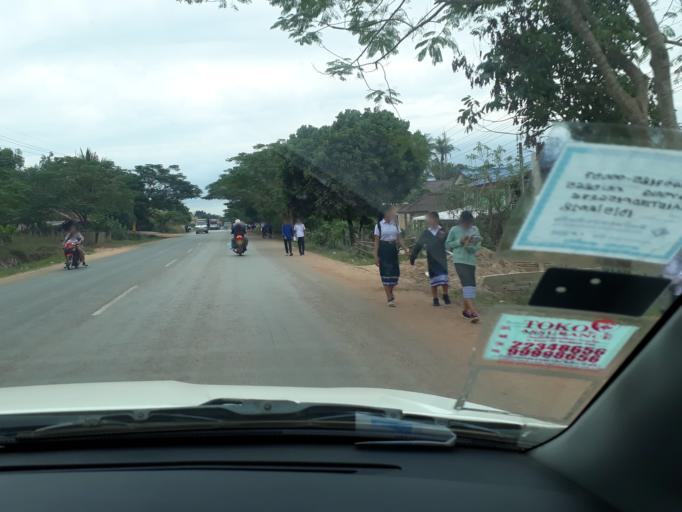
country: LA
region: Vientiane
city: Muang Phon-Hong
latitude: 18.3279
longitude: 102.4452
